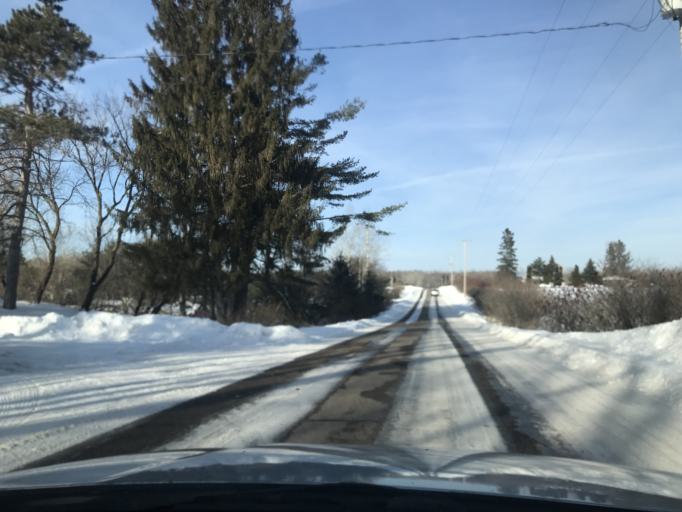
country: US
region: Wisconsin
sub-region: Menominee County
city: Legend Lake
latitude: 45.3123
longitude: -88.5217
